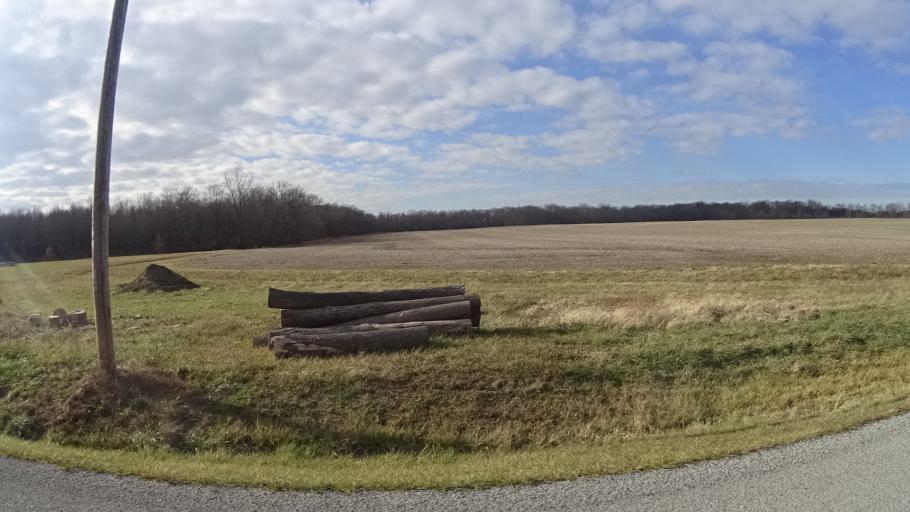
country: US
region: Ohio
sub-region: Lorain County
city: Wellington
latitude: 41.1379
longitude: -82.2910
